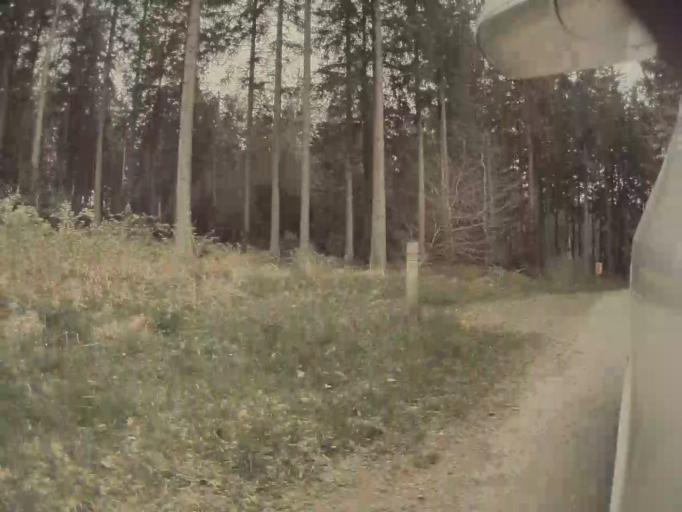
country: BE
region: Wallonia
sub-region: Province du Luxembourg
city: La Roche-en-Ardenne
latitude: 50.2370
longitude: 5.5951
